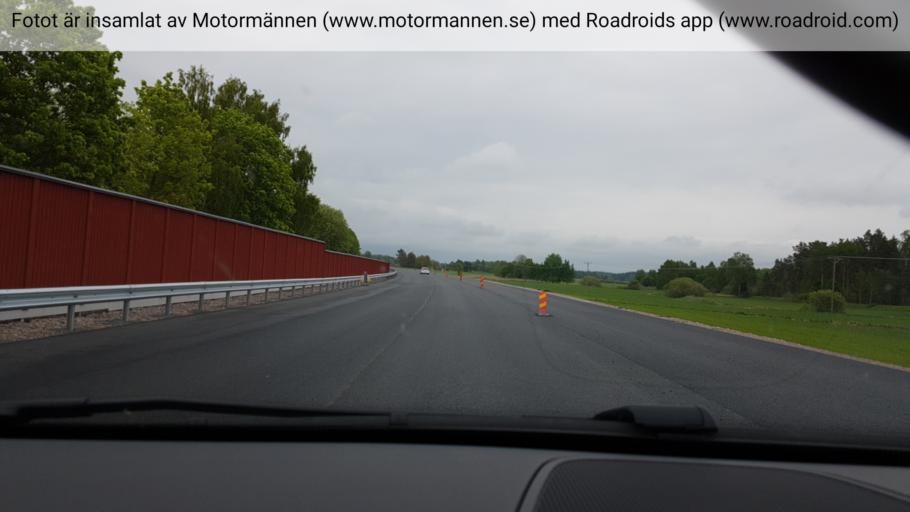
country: SE
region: Uppsala
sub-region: Osthammars Kommun
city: Gimo
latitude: 60.0639
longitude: 18.0838
